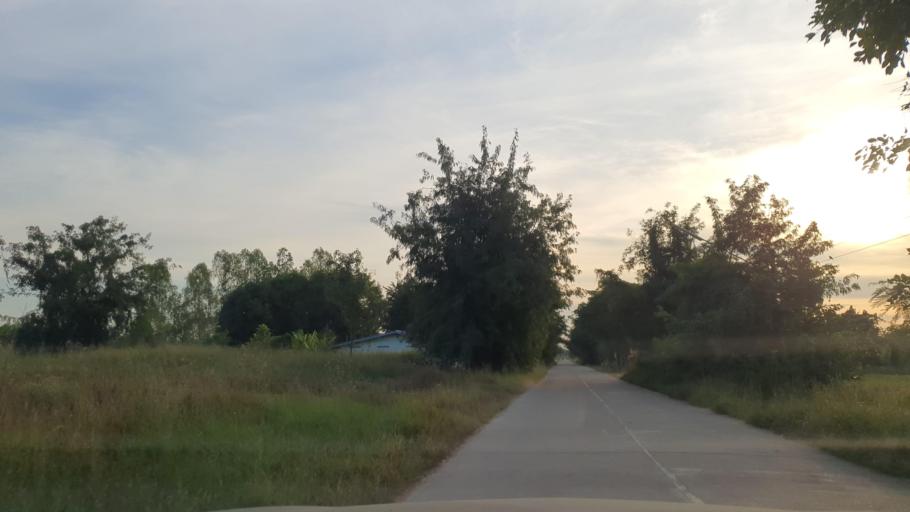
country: TH
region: Nakhon Sawan
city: Krok Phra
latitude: 15.6635
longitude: 100.0023
